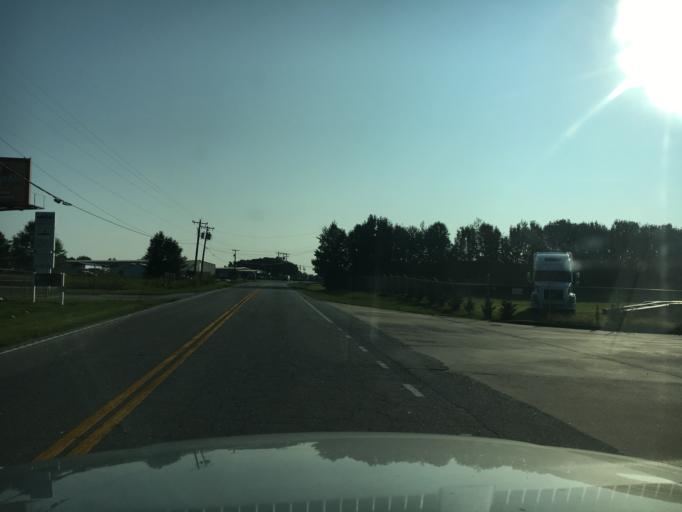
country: US
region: South Carolina
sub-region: Spartanburg County
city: Inman
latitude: 35.0830
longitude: -82.0583
